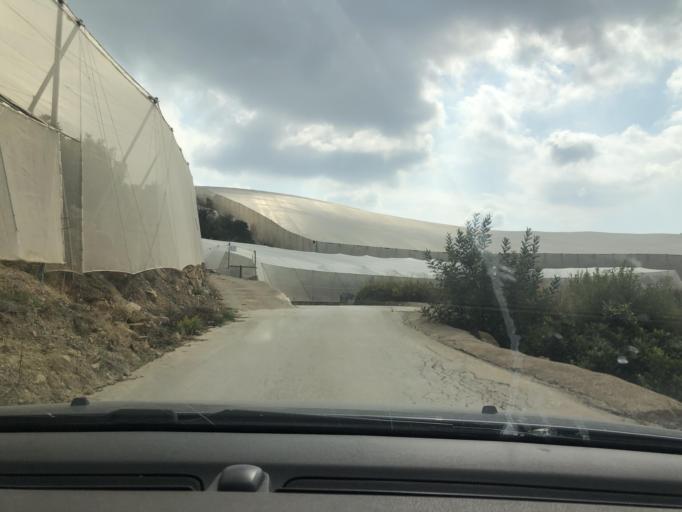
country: ES
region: Valencia
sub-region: Provincia de Alicante
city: Callosa d'En Sarria
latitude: 38.6541
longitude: -0.0901
